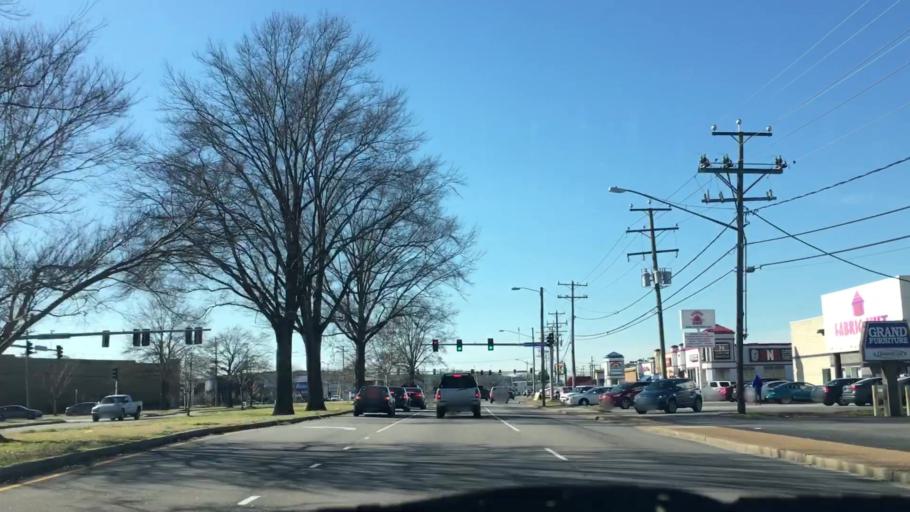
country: US
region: Virginia
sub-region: City of Norfolk
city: Norfolk
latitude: 36.9154
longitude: -76.2496
